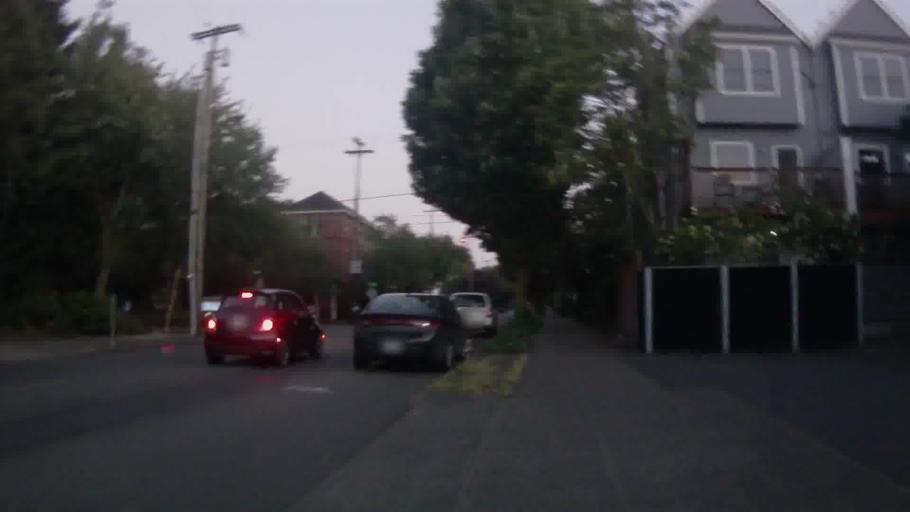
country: US
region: Oregon
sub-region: Multnomah County
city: Portland
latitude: 45.5358
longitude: -122.7030
